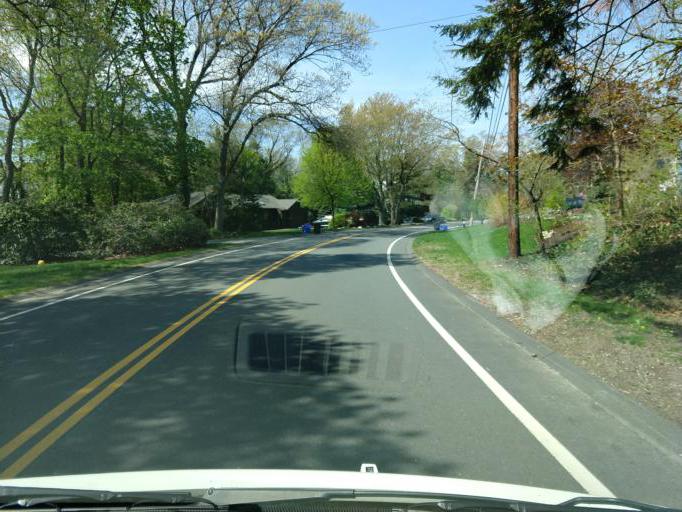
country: US
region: Massachusetts
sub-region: Middlesex County
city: Lexington
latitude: 42.4318
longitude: -71.2158
